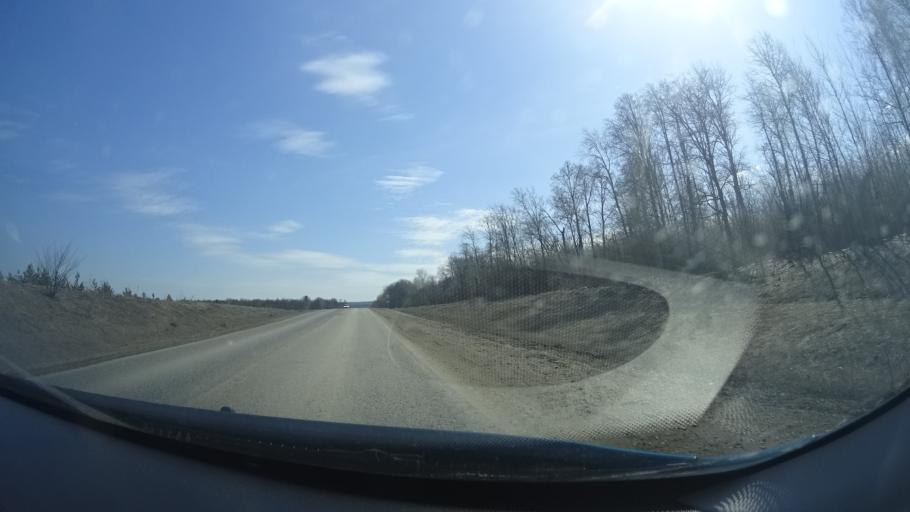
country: RU
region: Bashkortostan
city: Oktyabr'skiy
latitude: 54.4546
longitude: 53.5886
